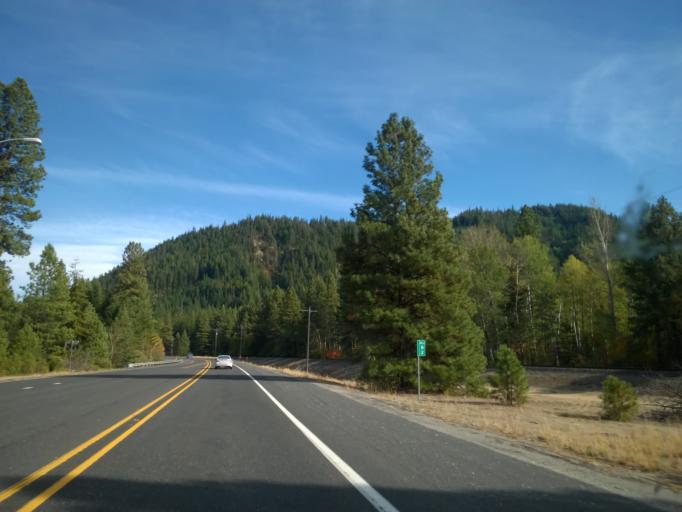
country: US
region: Washington
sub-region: Chelan County
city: Leavenworth
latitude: 47.7650
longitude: -120.7910
